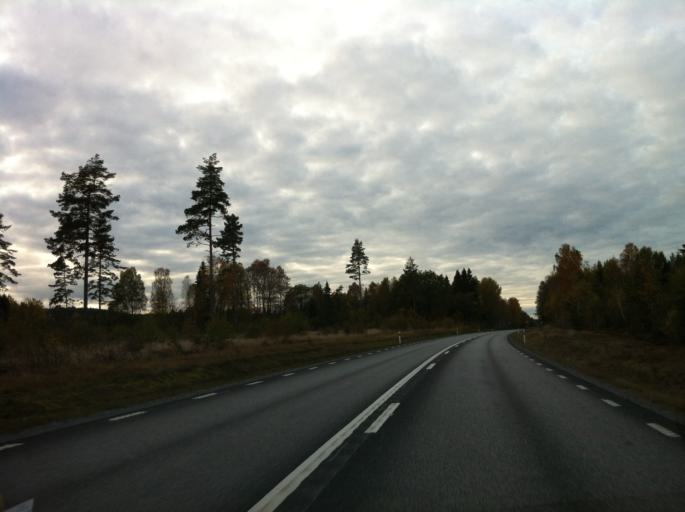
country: SE
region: OErebro
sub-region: Nora Kommun
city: Nora
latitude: 59.4698
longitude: 15.1314
